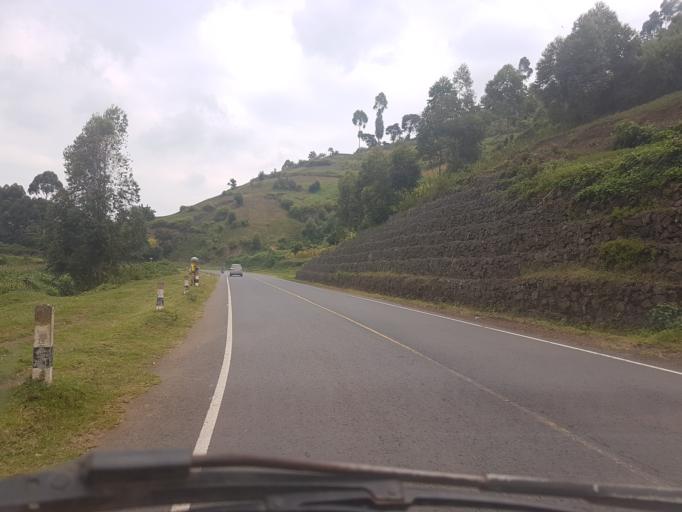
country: UG
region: Western Region
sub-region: Kisoro District
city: Kisoro
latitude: -1.2010
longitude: 29.8144
